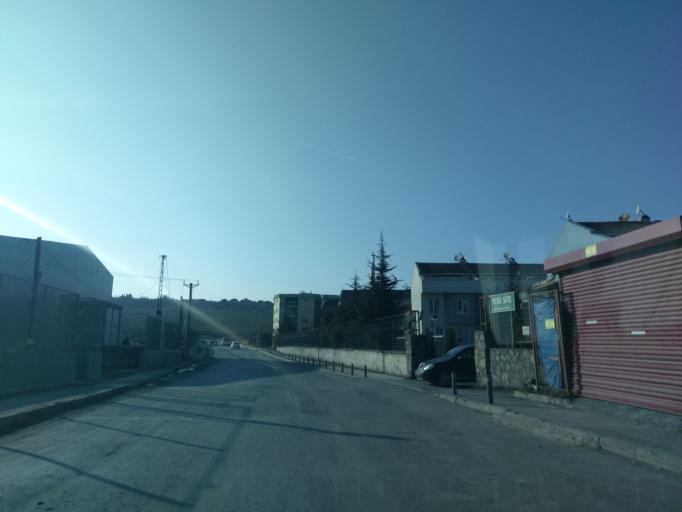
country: TR
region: Istanbul
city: Mahmutbey
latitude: 41.0292
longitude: 28.7676
